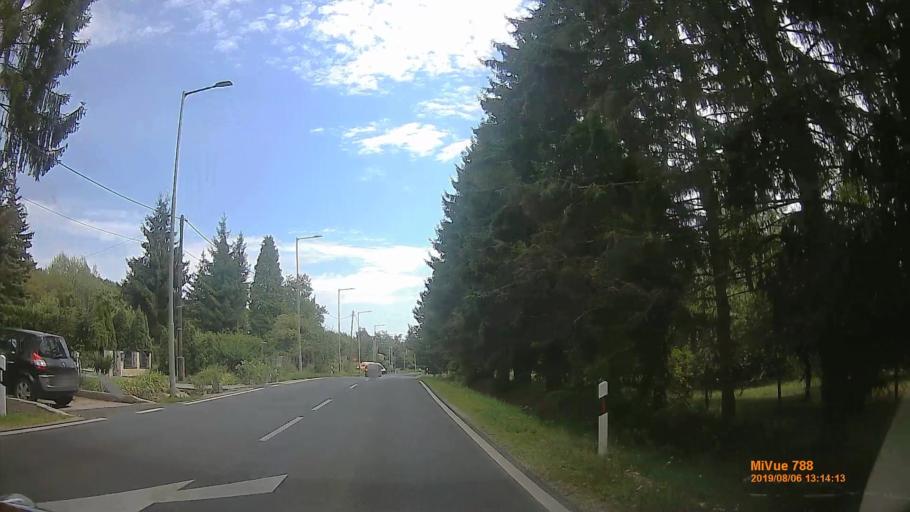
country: HU
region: Vas
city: Koszeg
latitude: 47.4054
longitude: 16.5308
